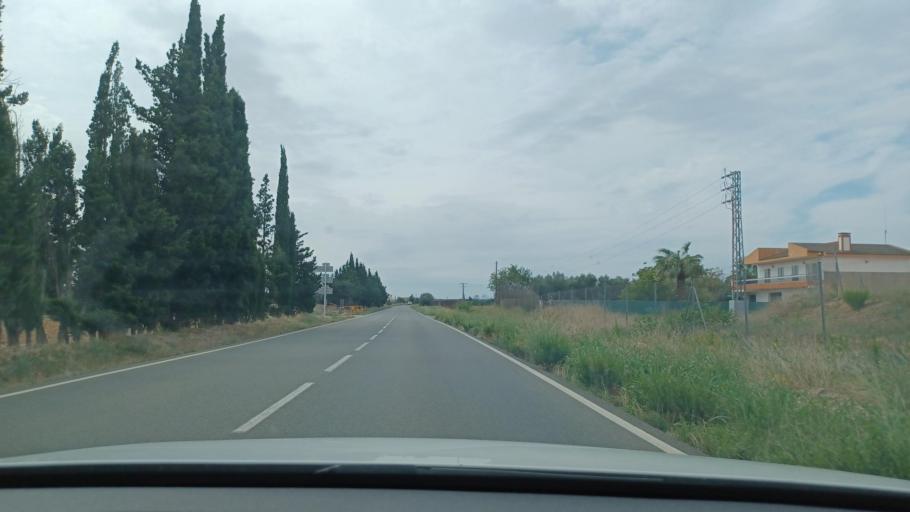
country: ES
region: Catalonia
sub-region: Provincia de Tarragona
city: Tortosa
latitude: 40.7699
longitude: 0.5106
